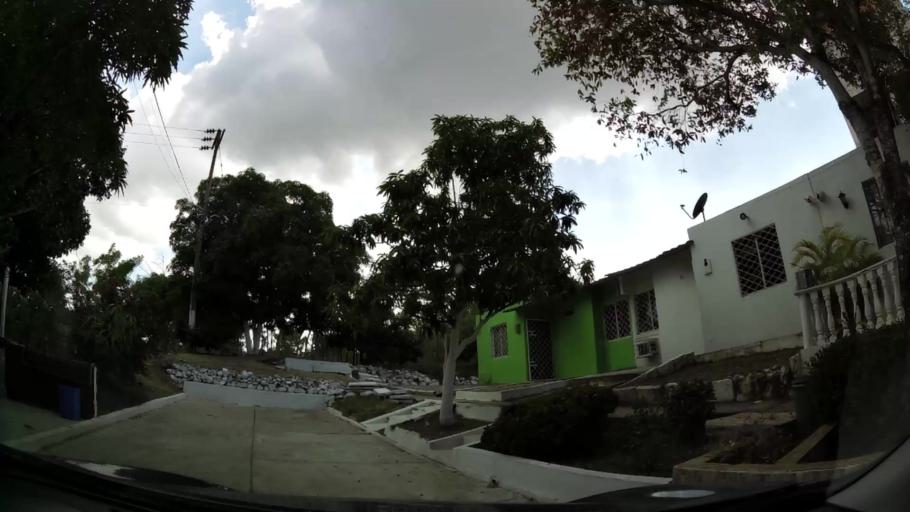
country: CO
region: Bolivar
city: Cartagena
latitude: 10.3689
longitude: -75.4614
